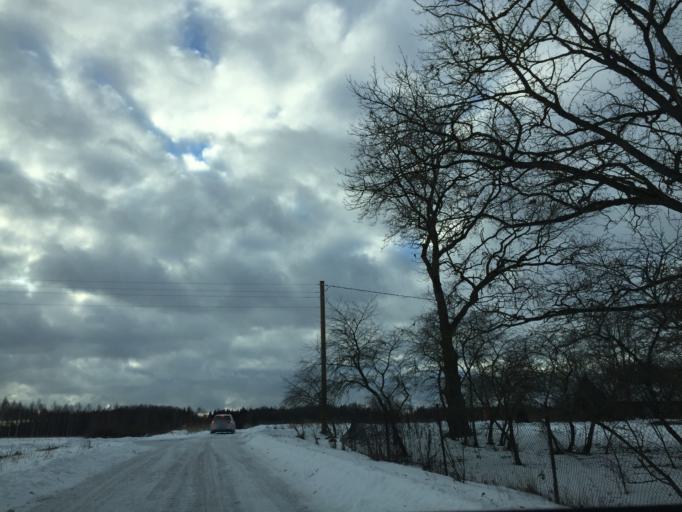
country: LV
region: Lielvarde
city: Lielvarde
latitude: 56.6236
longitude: 24.7402
